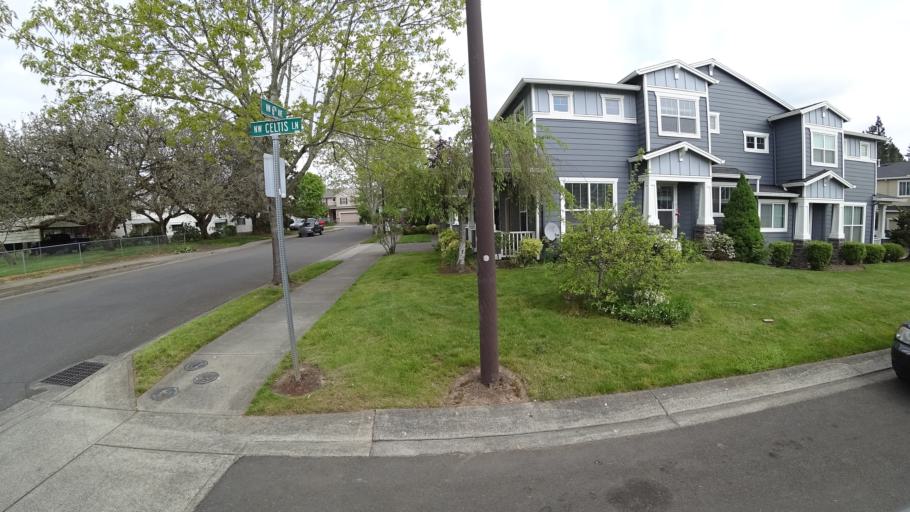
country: US
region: Oregon
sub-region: Washington County
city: Hillsboro
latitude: 45.5358
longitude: -122.9950
